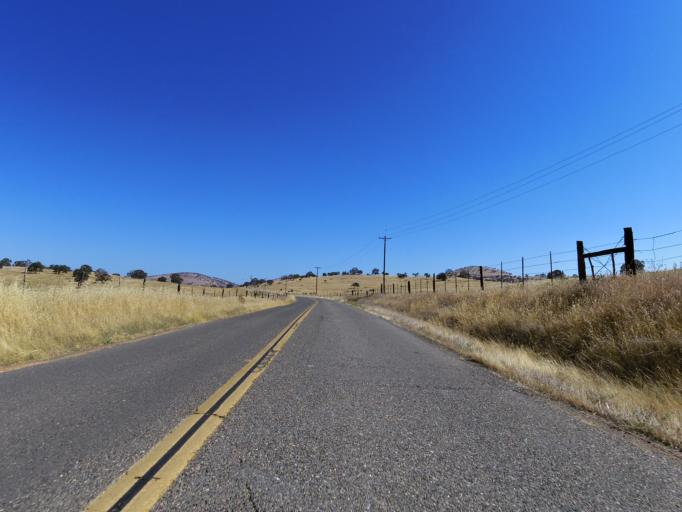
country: US
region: California
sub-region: Merced County
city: Planada
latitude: 37.5867
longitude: -120.3072
